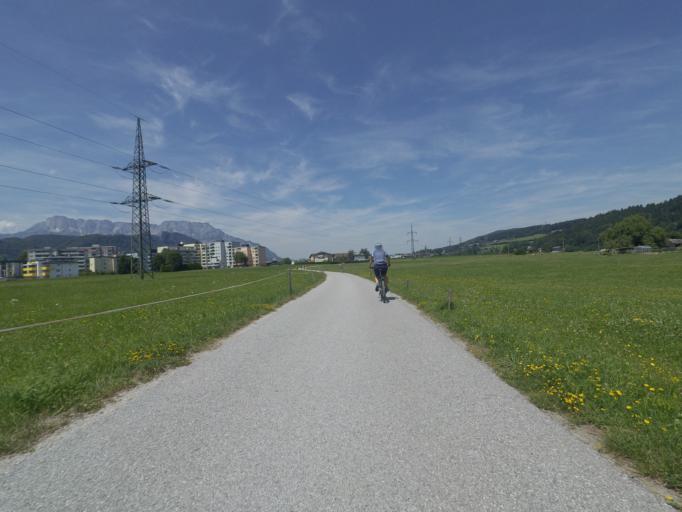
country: AT
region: Salzburg
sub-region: Politischer Bezirk Hallein
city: Adnet
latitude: 47.6776
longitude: 13.1188
